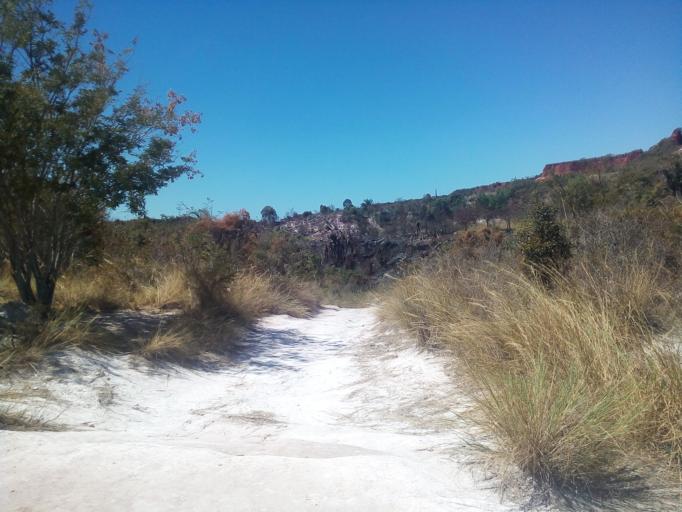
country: MG
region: Boeny
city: Mahajanga
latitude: -15.6337
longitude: 46.3500
